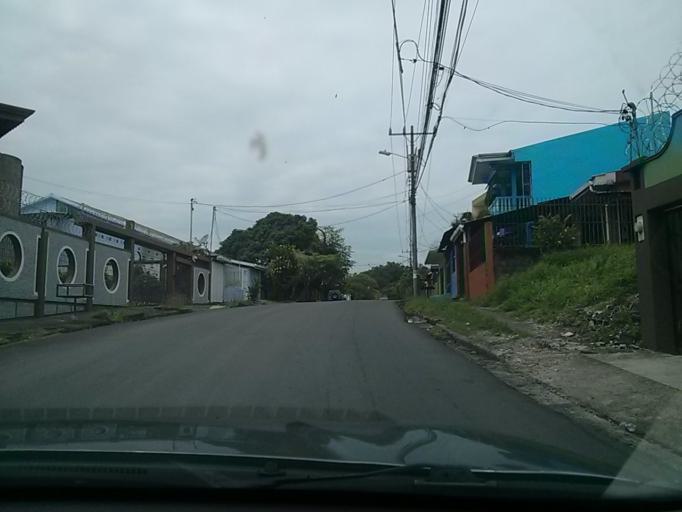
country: CR
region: Limon
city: Limon
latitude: 9.9988
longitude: -83.0351
